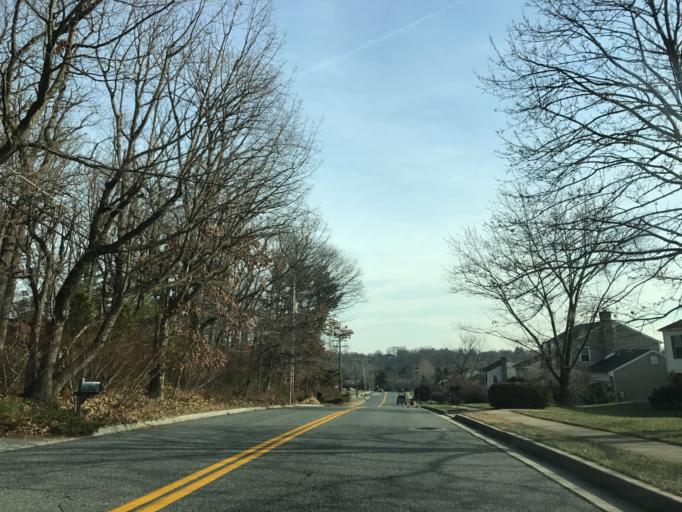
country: US
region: Maryland
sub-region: Baltimore County
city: Carney
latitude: 39.4089
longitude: -76.5405
